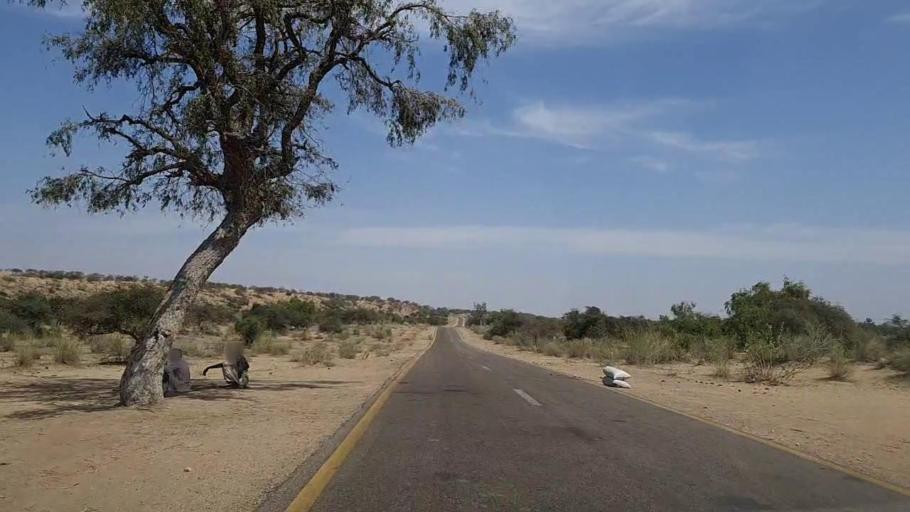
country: PK
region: Sindh
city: Mithi
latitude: 24.8260
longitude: 69.8264
